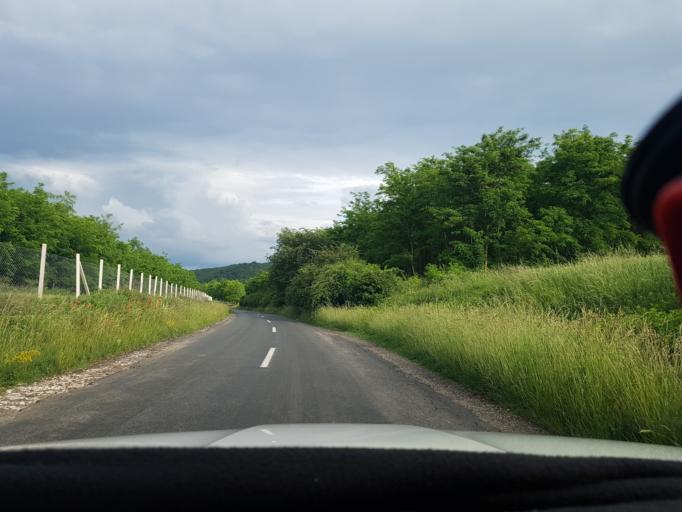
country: HU
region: Komarom-Esztergom
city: Nyergesujfalu
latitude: 47.7190
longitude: 18.5540
